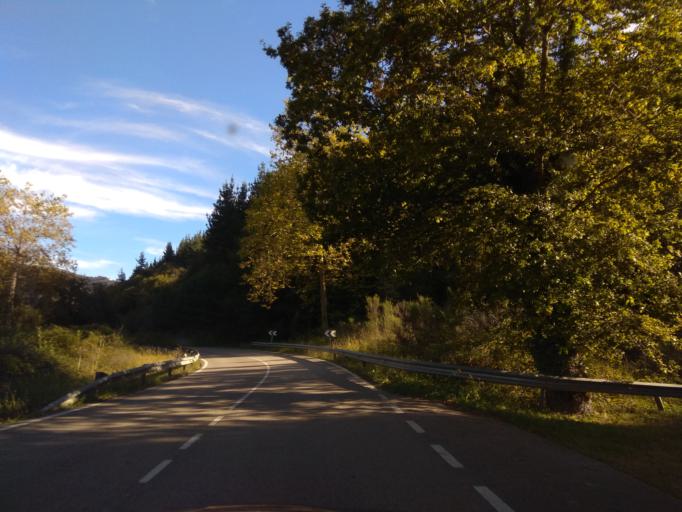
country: ES
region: Cantabria
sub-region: Provincia de Cantabria
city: Ruente
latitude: 43.2138
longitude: -4.3773
